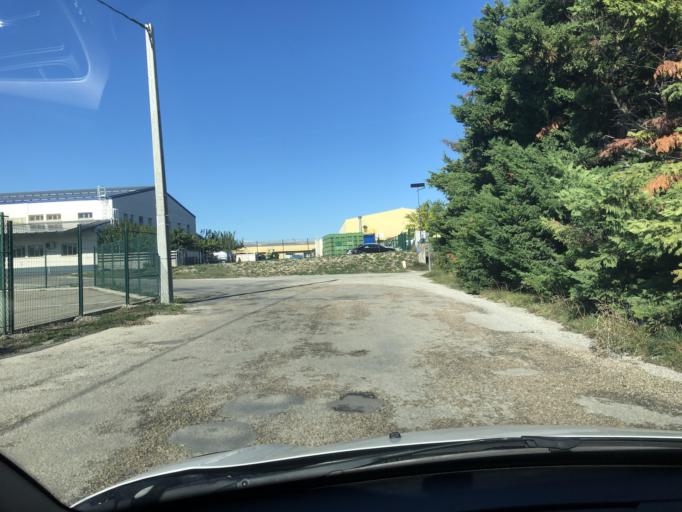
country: FR
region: Provence-Alpes-Cote d'Azur
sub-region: Departement du Vaucluse
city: Carpentras
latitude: 44.0349
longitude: 5.0444
